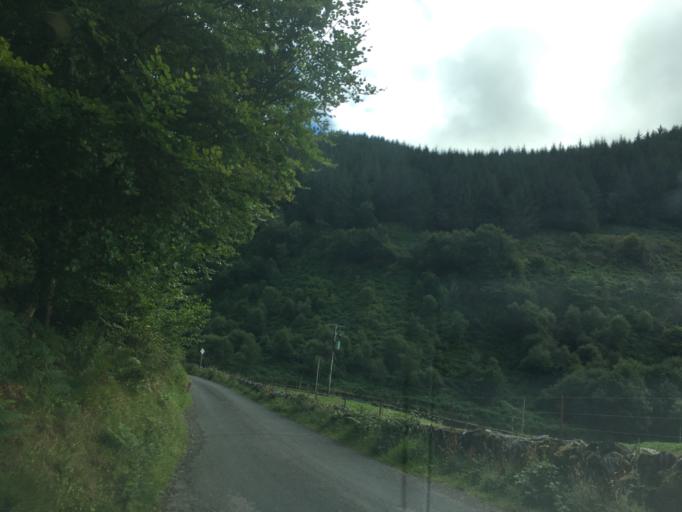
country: GB
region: Scotland
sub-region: Argyll and Bute
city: Ardrishaig
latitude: 56.0863
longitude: -5.5600
